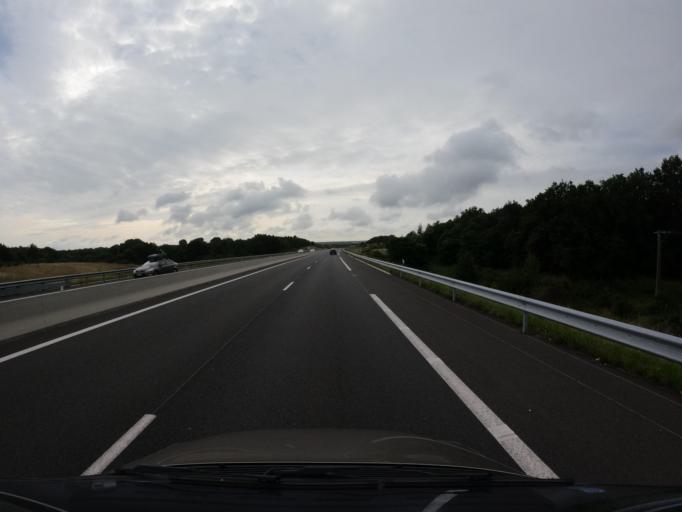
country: FR
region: Centre
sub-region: Departement d'Indre-et-Loire
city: Langeais
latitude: 47.3413
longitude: 0.4227
